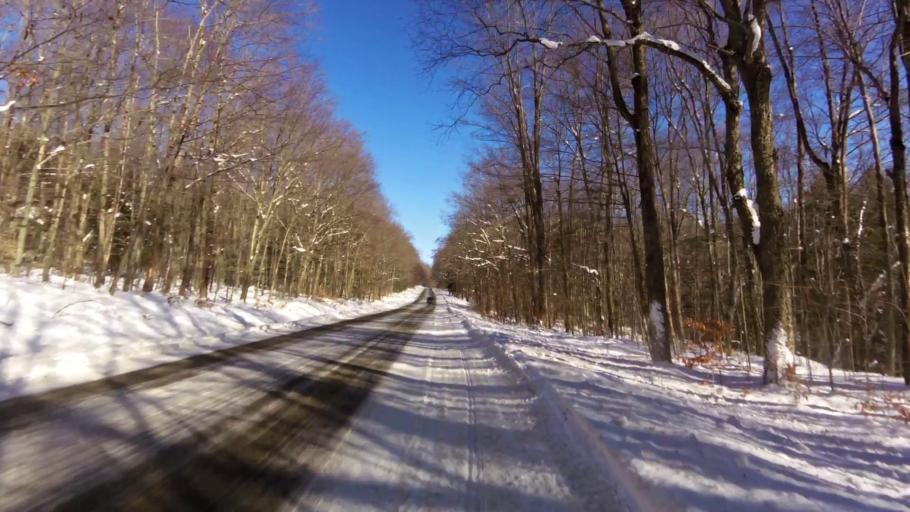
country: US
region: New York
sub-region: Cattaraugus County
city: Salamanca
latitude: 42.1162
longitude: -78.7356
